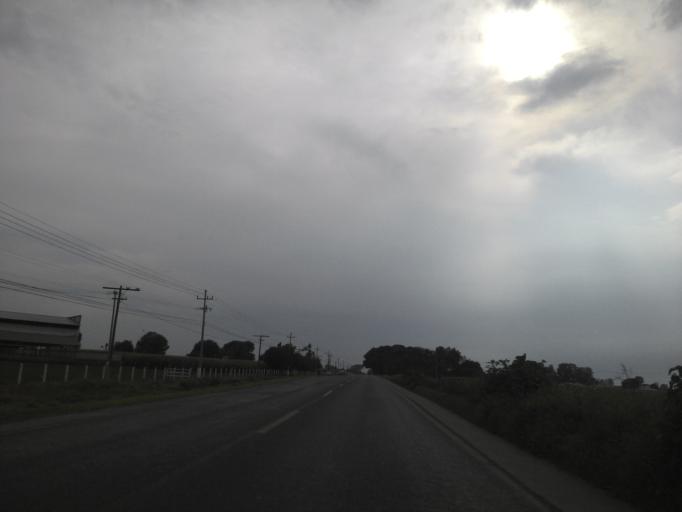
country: MX
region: Jalisco
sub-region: Acatic
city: Tierras Coloradas
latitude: 20.7295
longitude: -102.8719
